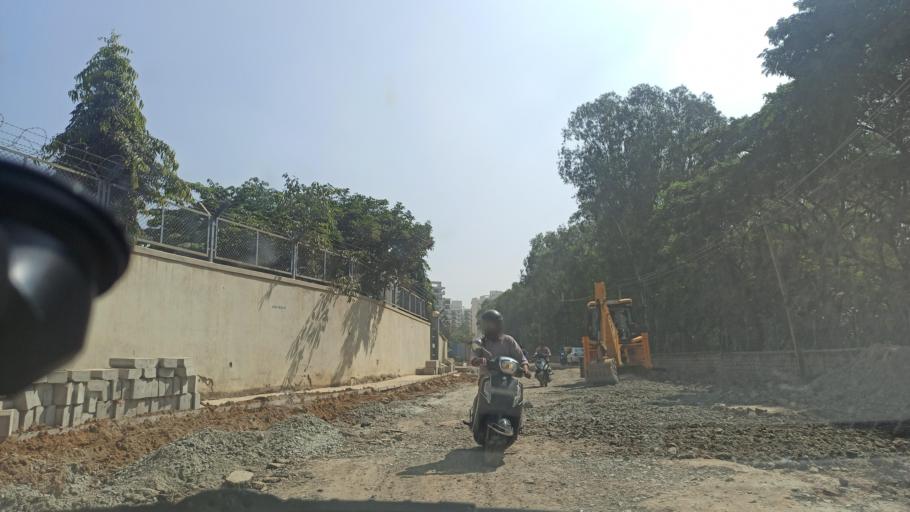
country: IN
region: Karnataka
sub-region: Bangalore Urban
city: Bangalore
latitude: 12.9185
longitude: 77.6862
